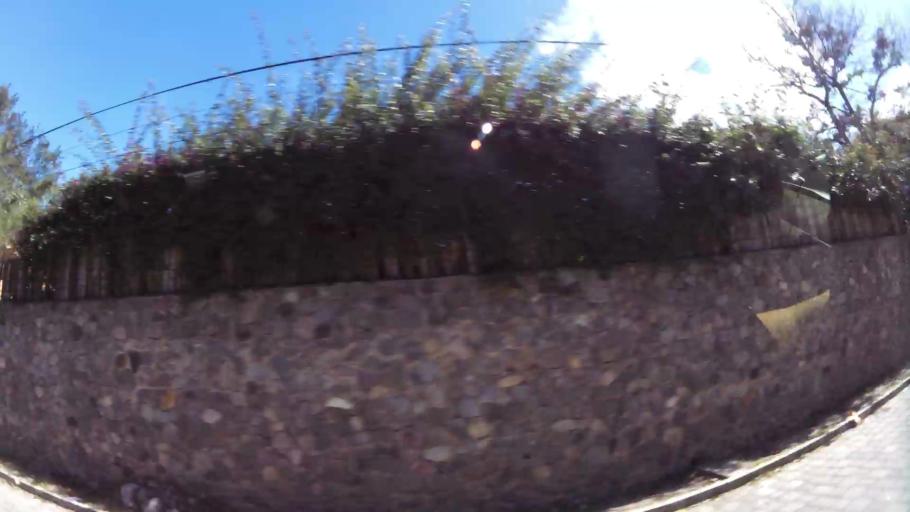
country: GT
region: Solola
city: Panajachel
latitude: 14.7411
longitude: -91.1545
